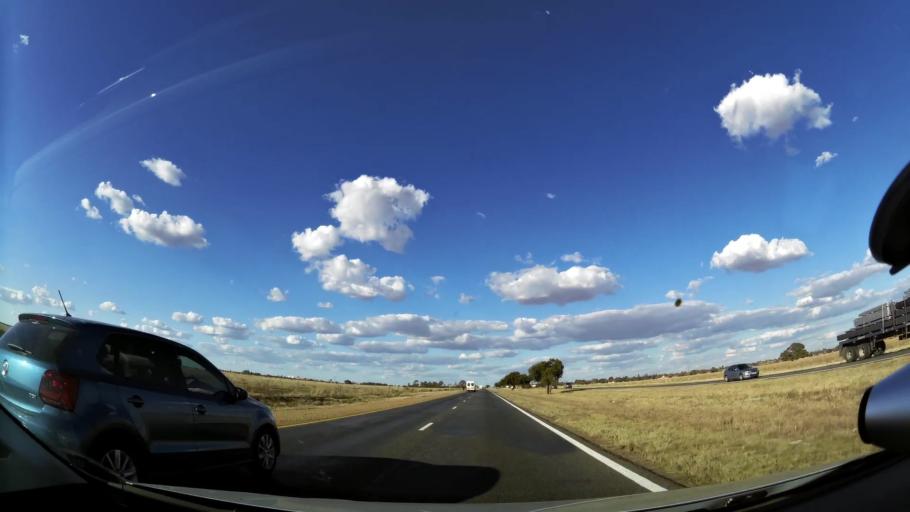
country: ZA
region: North-West
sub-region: Dr Kenneth Kaunda District Municipality
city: Stilfontein
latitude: -26.8443
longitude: 26.7315
